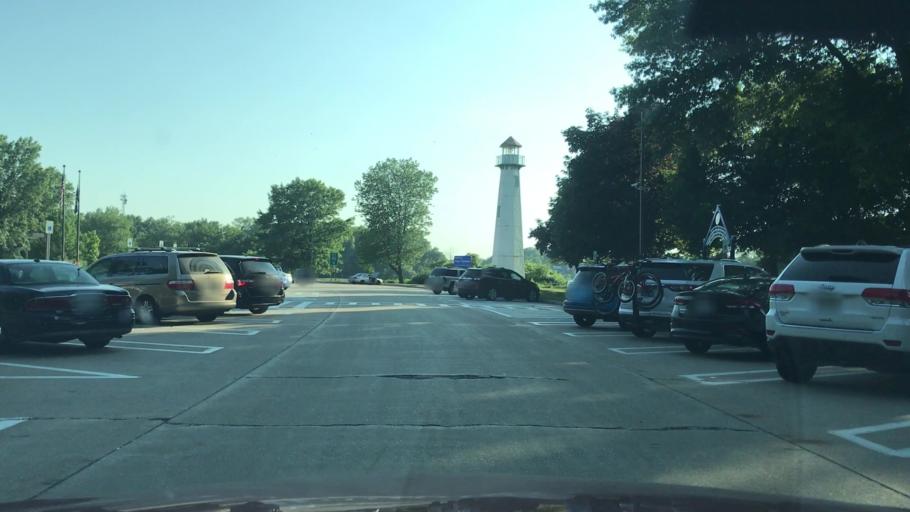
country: US
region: Michigan
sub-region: Berrien County
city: New Buffalo
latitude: 41.7655
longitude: -86.7406
